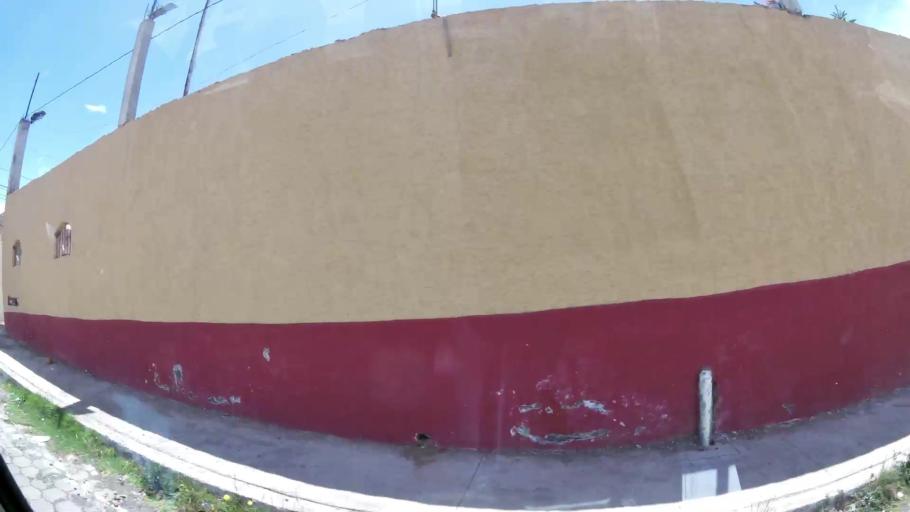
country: EC
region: Tungurahua
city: Ambato
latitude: -1.2873
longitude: -78.6044
